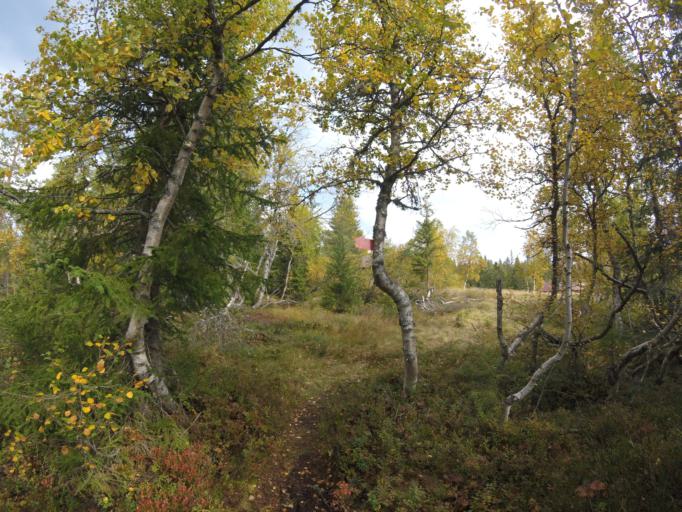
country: NO
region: Buskerud
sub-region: Rollag
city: Rollag
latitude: 59.8167
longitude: 9.3398
